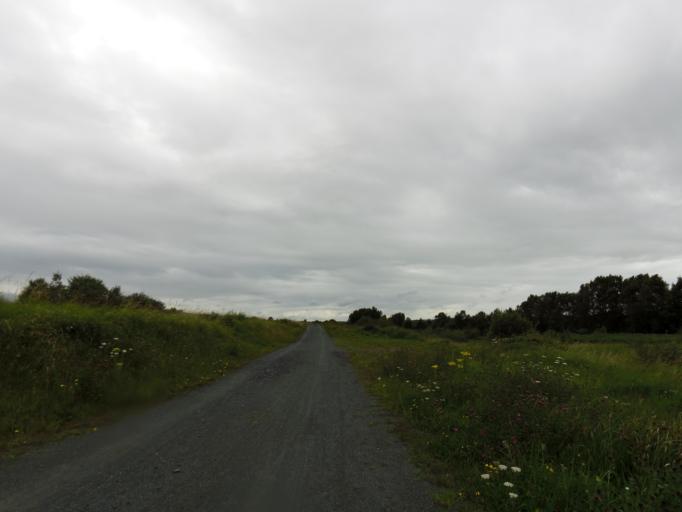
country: IE
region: Leinster
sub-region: An Iarmhi
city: Moate
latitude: 53.5810
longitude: -7.6088
